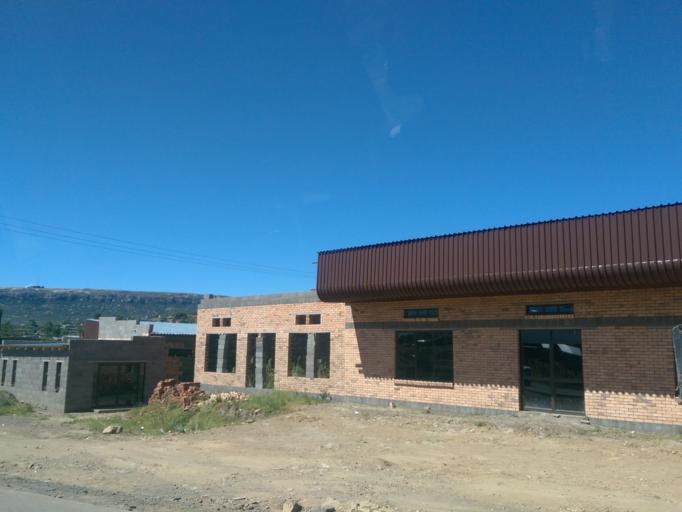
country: LS
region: Maseru
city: Maseru
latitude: -29.3800
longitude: 27.5592
